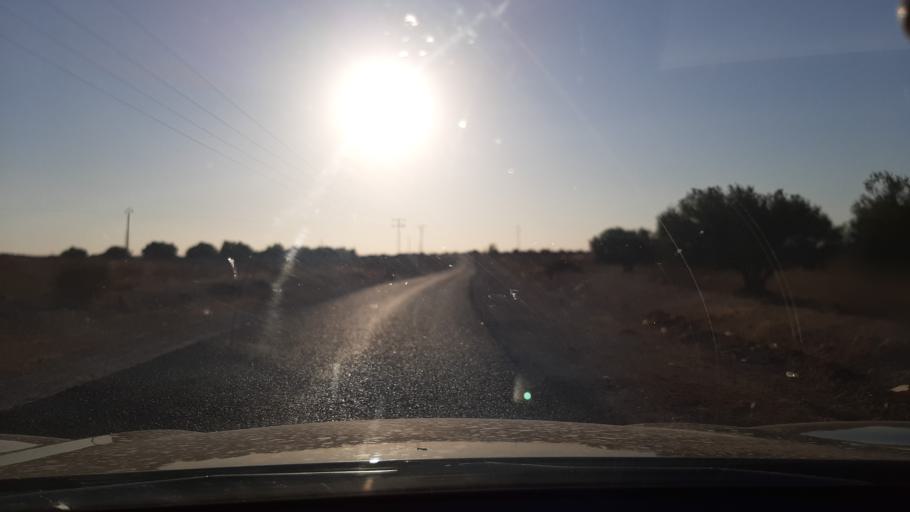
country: TN
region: Qabis
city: Matmata
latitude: 33.6165
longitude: 10.2424
